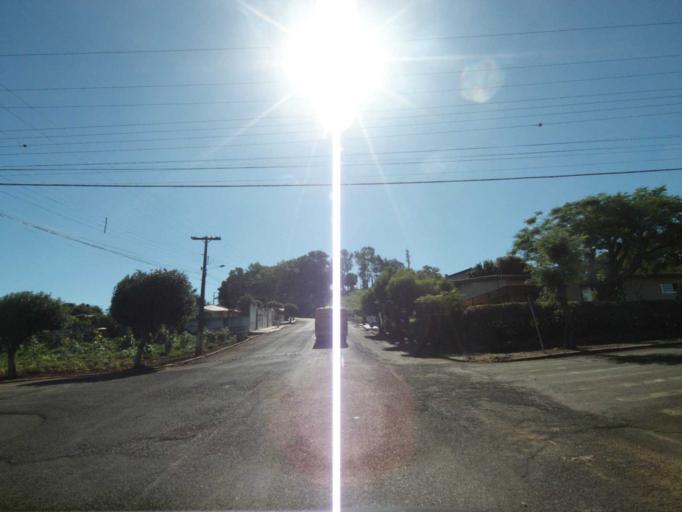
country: BR
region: Parana
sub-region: Coronel Vivida
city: Coronel Vivida
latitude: -25.9598
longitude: -52.8177
